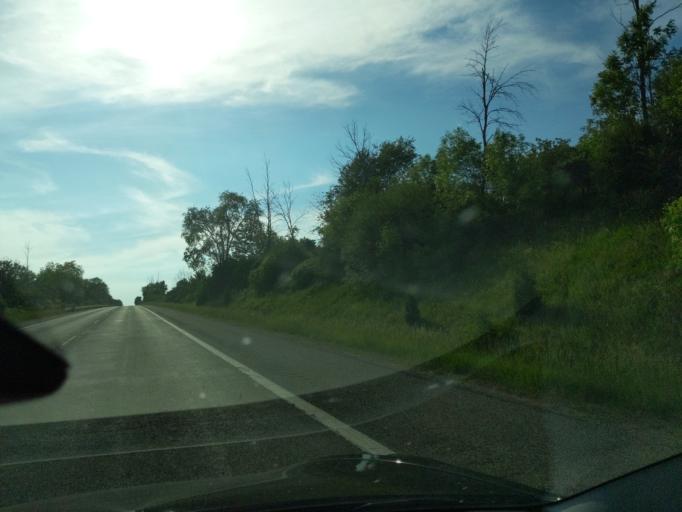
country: US
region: Michigan
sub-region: Barry County
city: Nashville
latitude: 42.6034
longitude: -85.1284
